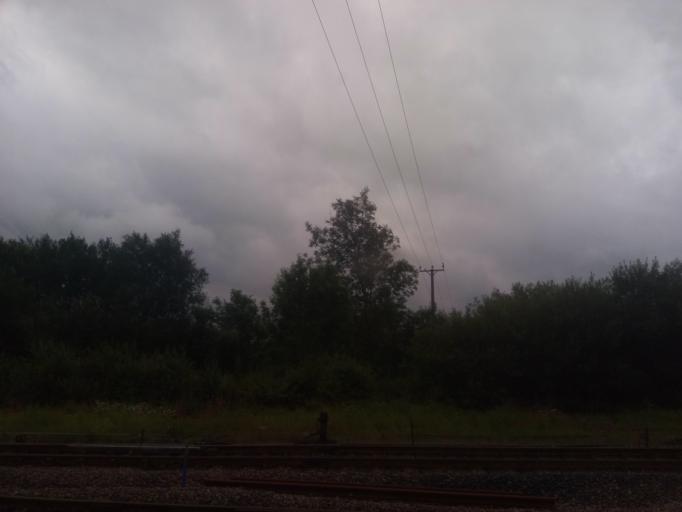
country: GB
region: England
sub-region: North Yorkshire
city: Settle
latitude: 54.0096
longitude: -2.2251
